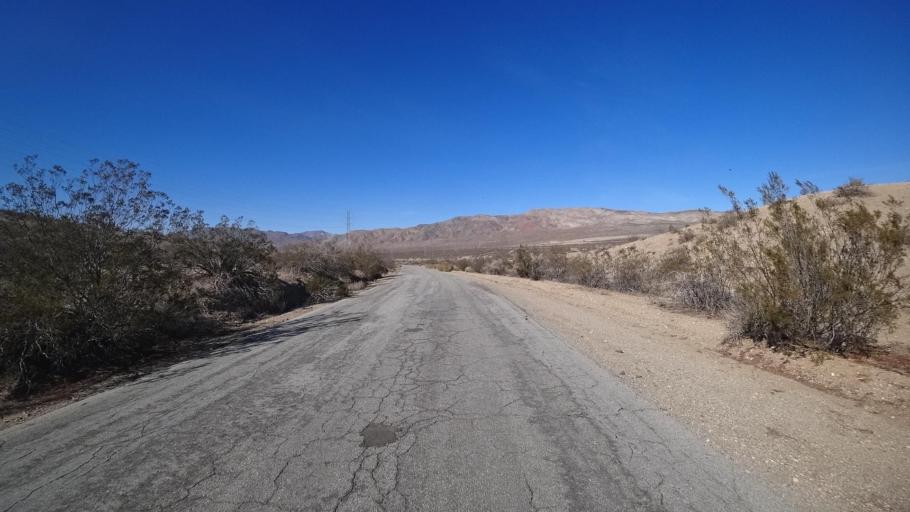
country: US
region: California
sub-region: Kern County
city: Ridgecrest
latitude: 35.4145
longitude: -117.6869
